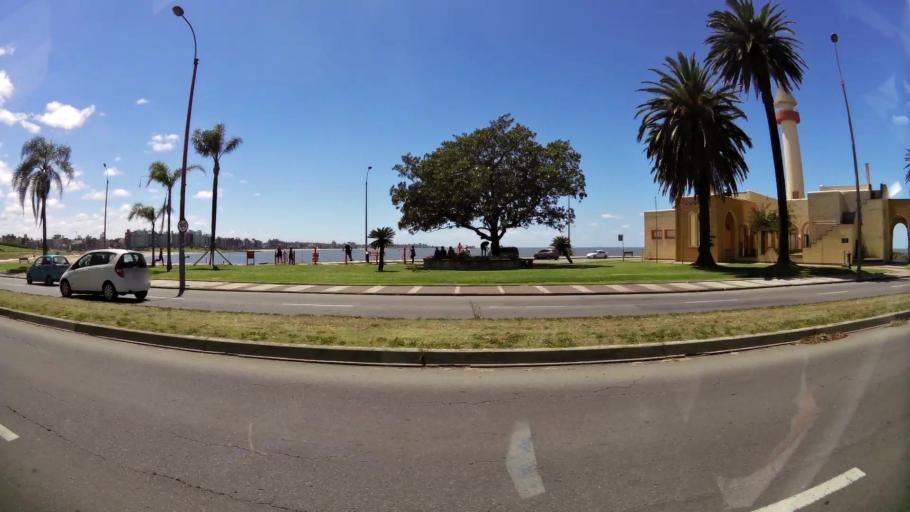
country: UY
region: Montevideo
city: Montevideo
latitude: -34.9031
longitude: -56.1241
